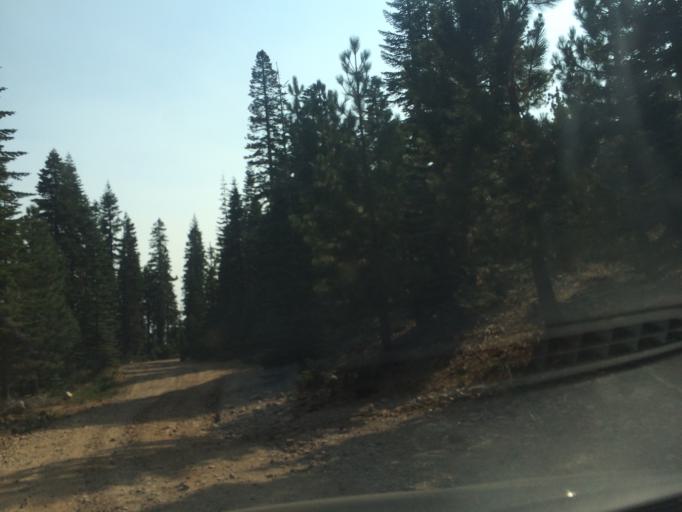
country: US
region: California
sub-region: Sierra County
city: Downieville
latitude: 39.4031
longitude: -120.6515
